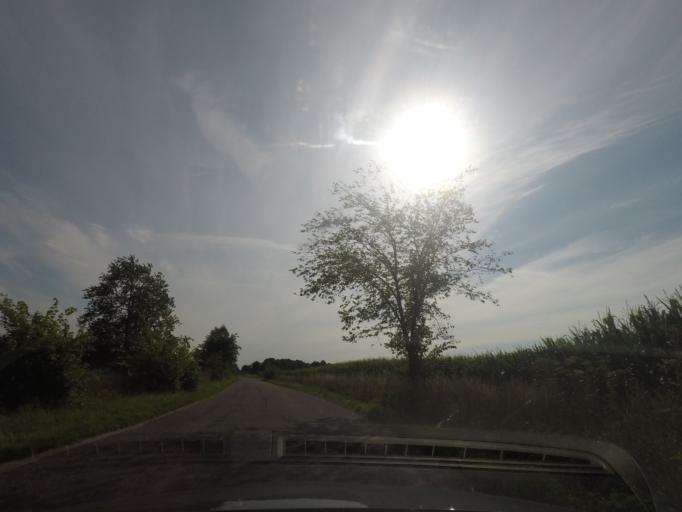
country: PL
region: Pomeranian Voivodeship
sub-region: Powiat slupski
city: Smoldzino
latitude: 54.6298
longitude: 17.2465
